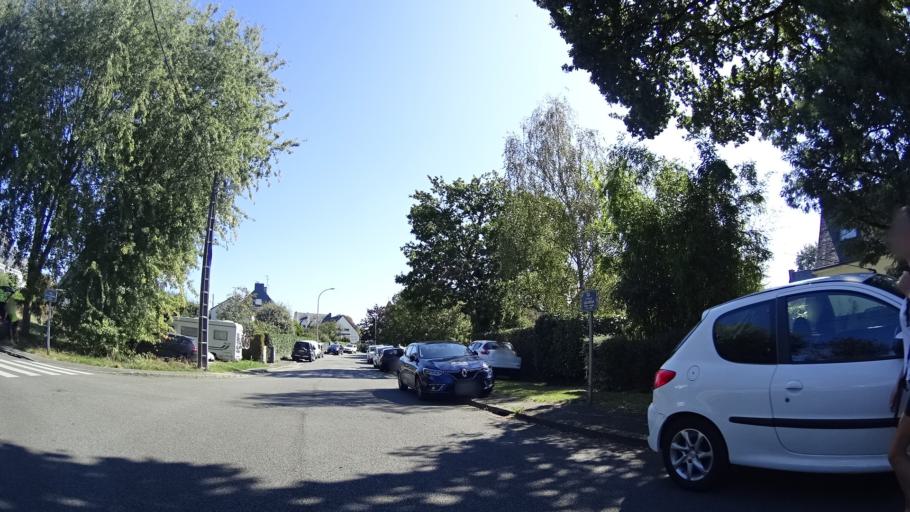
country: FR
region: Brittany
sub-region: Departement du Morbihan
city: Vannes
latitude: 47.6434
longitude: -2.7681
